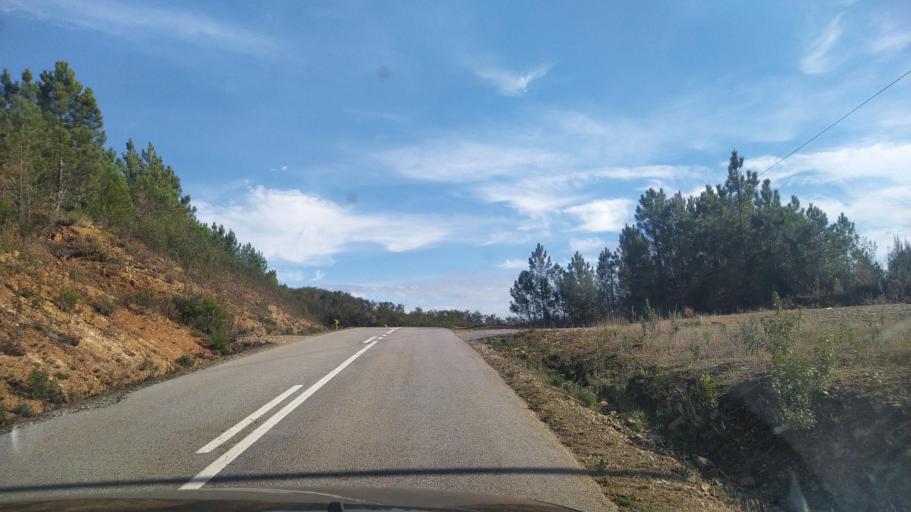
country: PT
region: Castelo Branco
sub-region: Concelho do Fundao
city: Aldeia de Joanes
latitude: 40.1765
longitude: -7.6832
